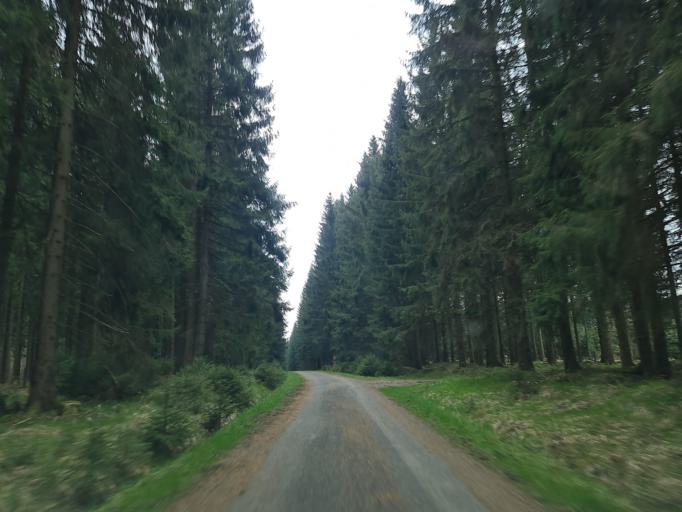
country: DE
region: Saxony
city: Grunbach
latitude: 50.4527
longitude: 12.3855
